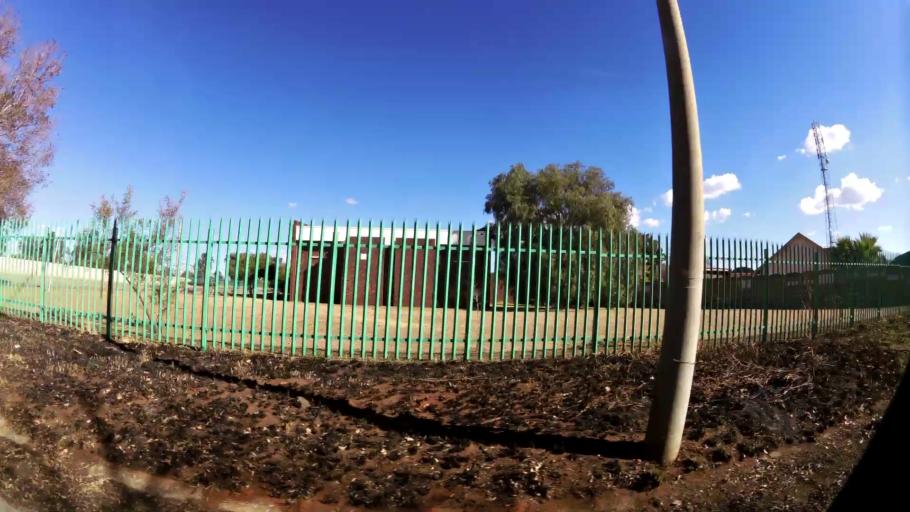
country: ZA
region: Gauteng
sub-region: West Rand District Municipality
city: Carletonville
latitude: -26.3616
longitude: 27.3723
